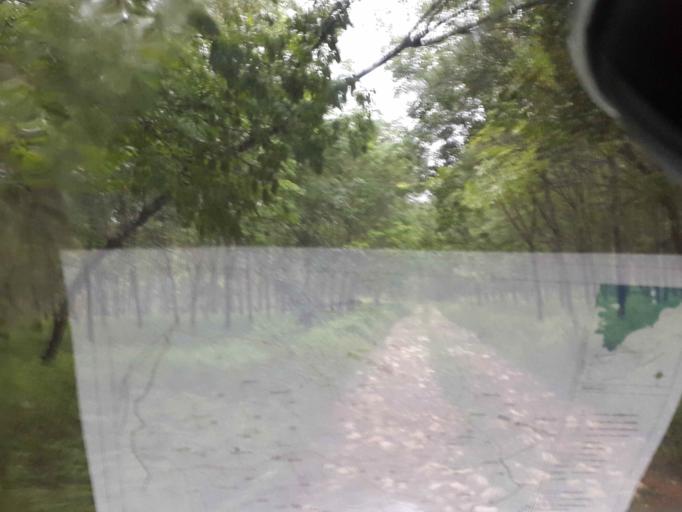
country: ID
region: Lampung
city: Kedaton
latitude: -5.3854
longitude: 105.3533
